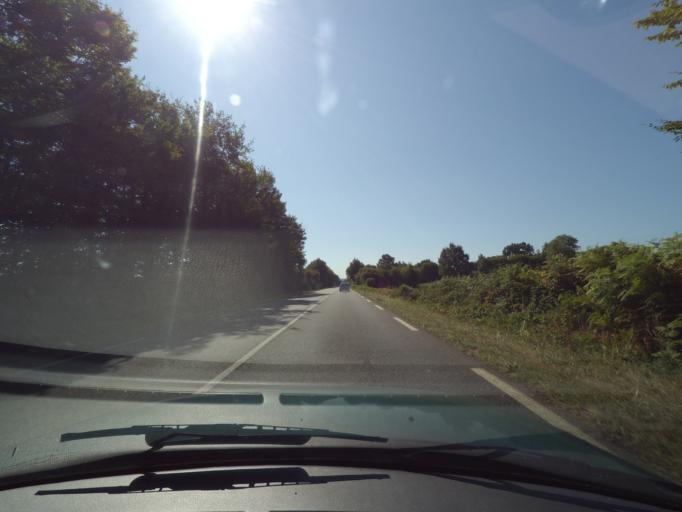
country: FR
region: Limousin
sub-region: Departement de la Haute-Vienne
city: Bussiere-Poitevine
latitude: 46.1842
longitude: 0.9346
